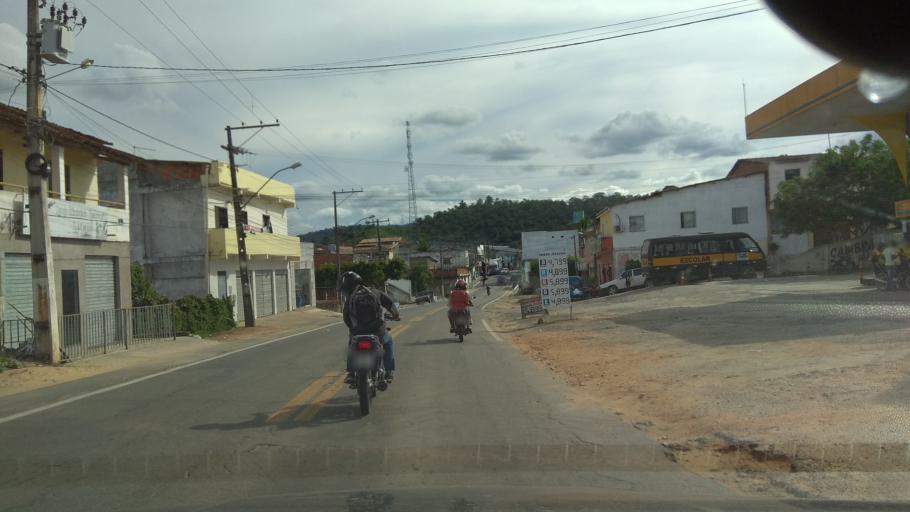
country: BR
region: Bahia
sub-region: Jitauna
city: Jitauna
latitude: -14.0172
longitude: -39.8857
